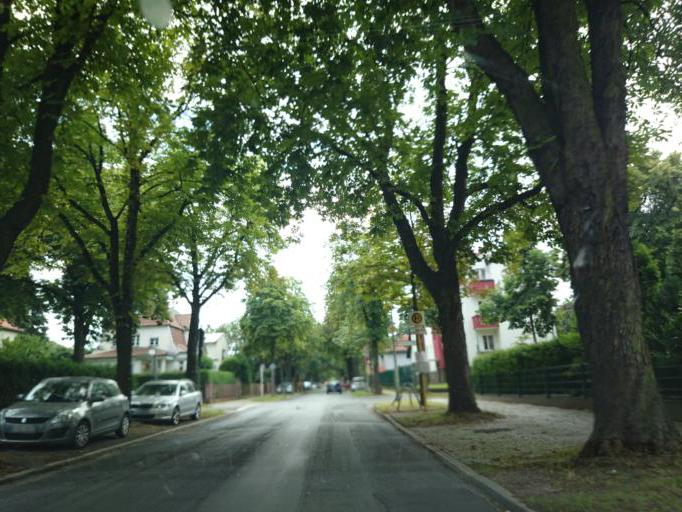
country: DE
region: Berlin
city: Lankwitz
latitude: 52.4205
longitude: 13.3504
